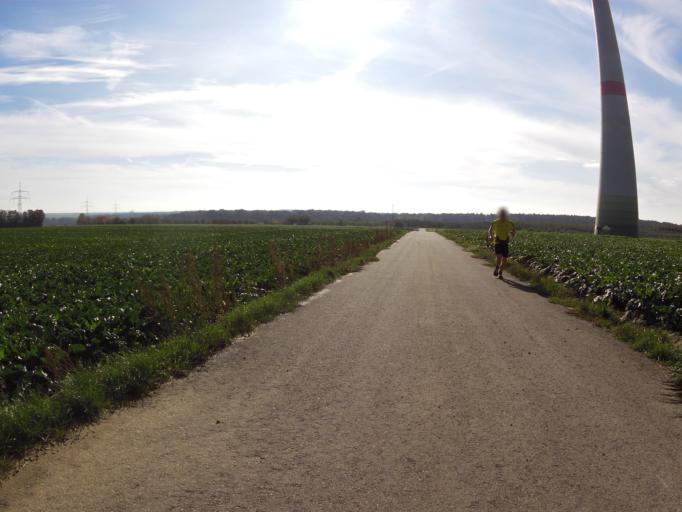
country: DE
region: Bavaria
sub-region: Regierungsbezirk Unterfranken
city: Sommerhausen
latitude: 49.7155
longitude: 10.0541
